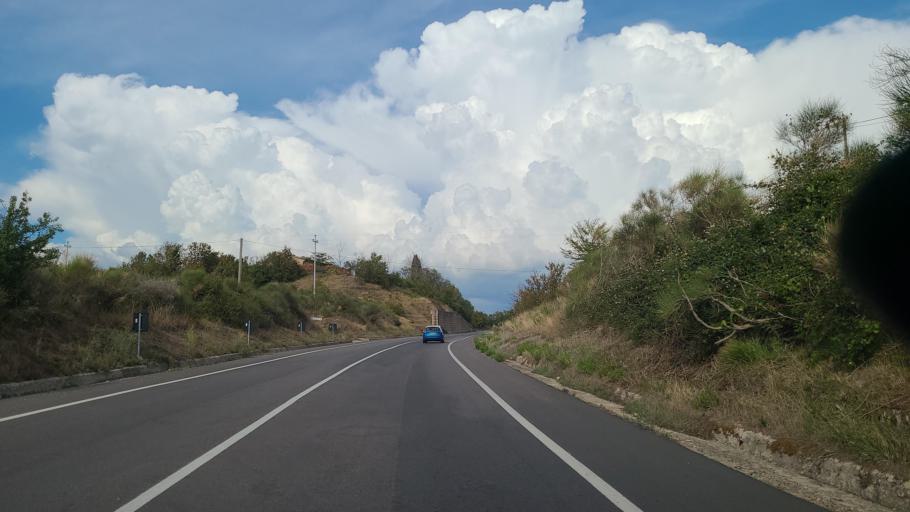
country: IT
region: Tuscany
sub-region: Province of Pisa
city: Volterra
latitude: 43.3857
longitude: 10.9393
